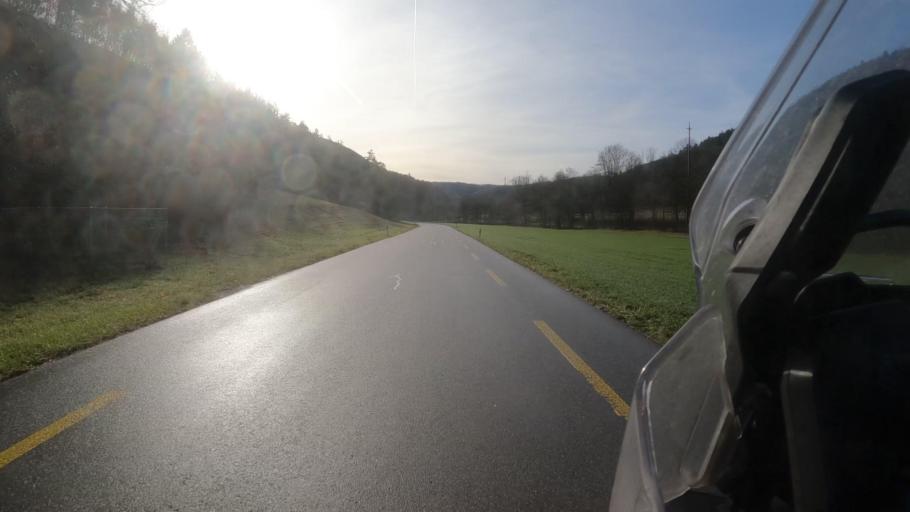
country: CH
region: Schaffhausen
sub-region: Bezirk Reiat
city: Stetten
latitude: 47.7761
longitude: 8.6175
